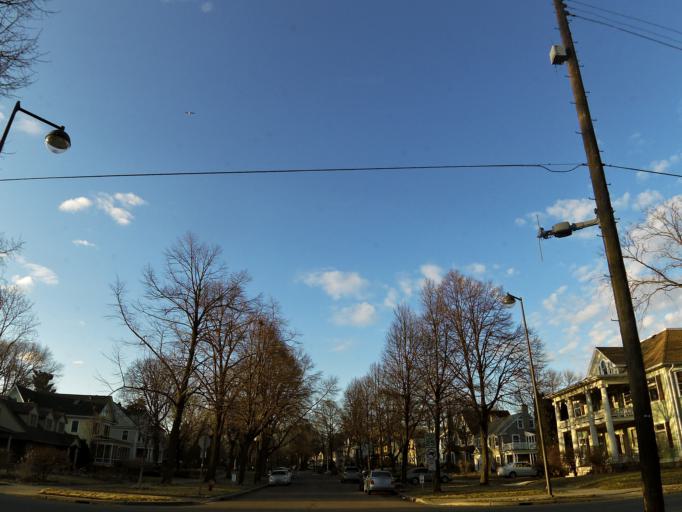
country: US
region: Minnesota
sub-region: Hennepin County
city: Saint Louis Park
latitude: 44.9274
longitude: -93.3114
